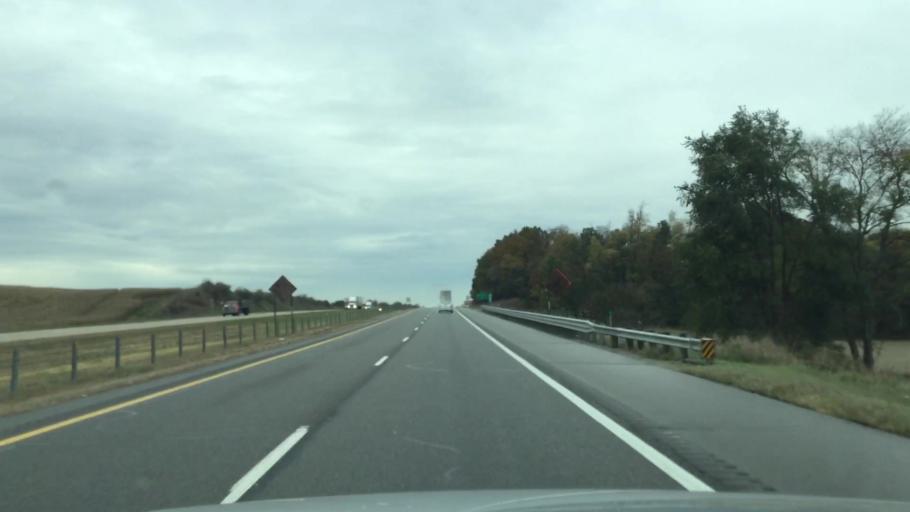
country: US
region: Michigan
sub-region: Calhoun County
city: Albion
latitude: 42.2834
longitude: -84.8528
